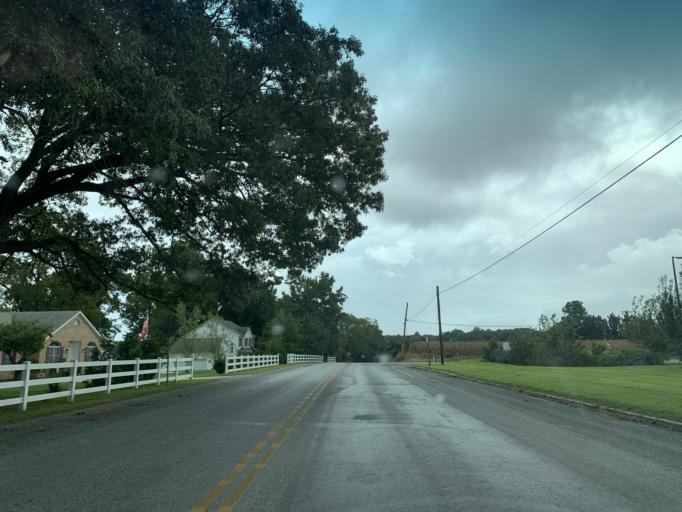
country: US
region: Maryland
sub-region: Caroline County
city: Denton
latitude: 38.9083
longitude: -75.8394
